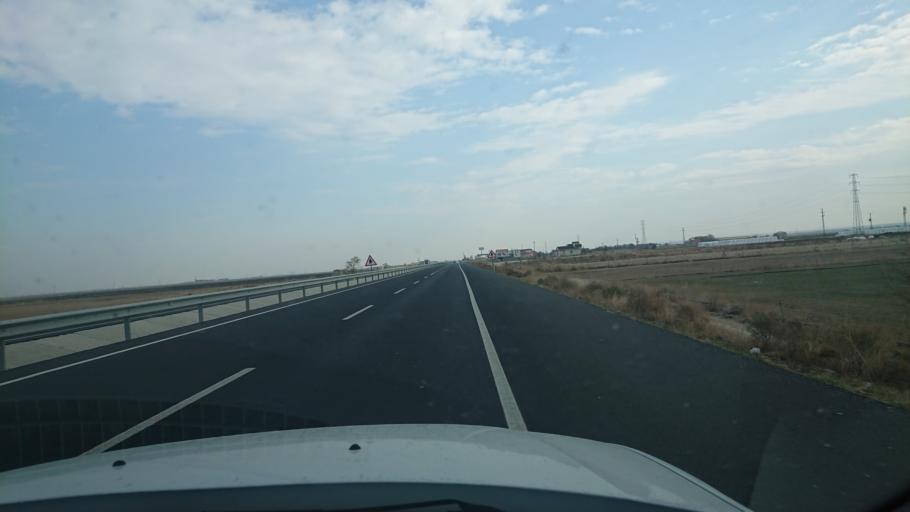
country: TR
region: Aksaray
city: Yesilova
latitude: 38.3006
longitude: 33.7980
